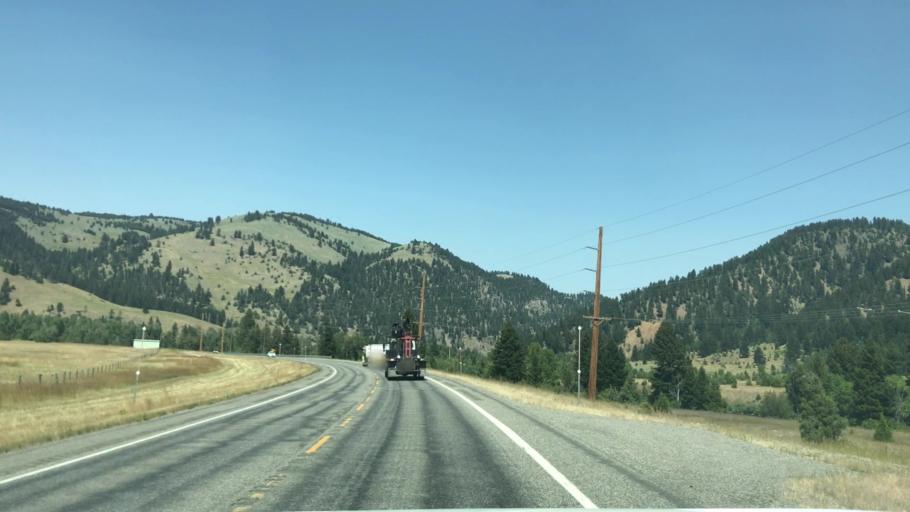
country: US
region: Montana
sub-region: Gallatin County
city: Four Corners
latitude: 45.4869
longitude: -111.2708
